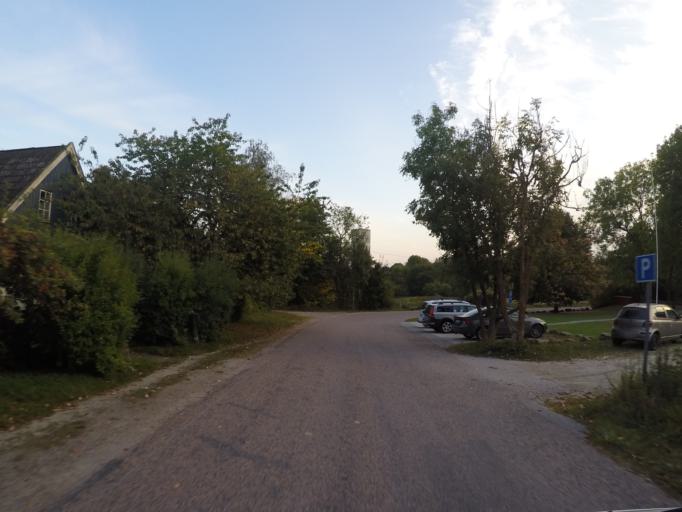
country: SE
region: Skane
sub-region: Lunds Kommun
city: Genarp
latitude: 55.6737
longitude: 13.3588
